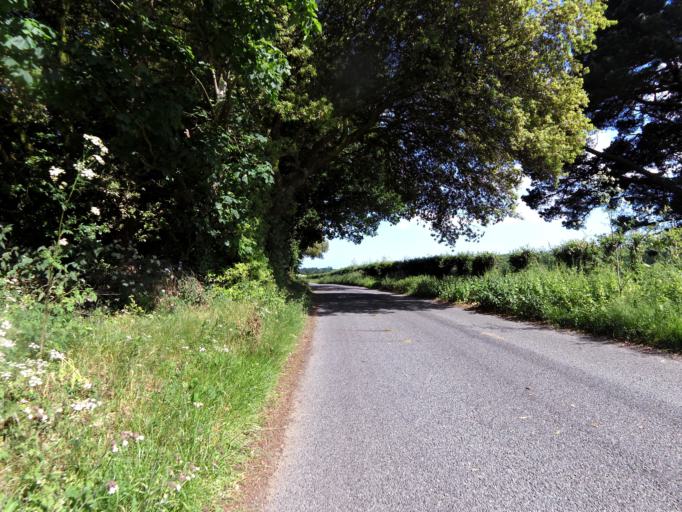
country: GB
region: England
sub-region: Suffolk
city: Kesgrave
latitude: 52.0110
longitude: 1.2349
